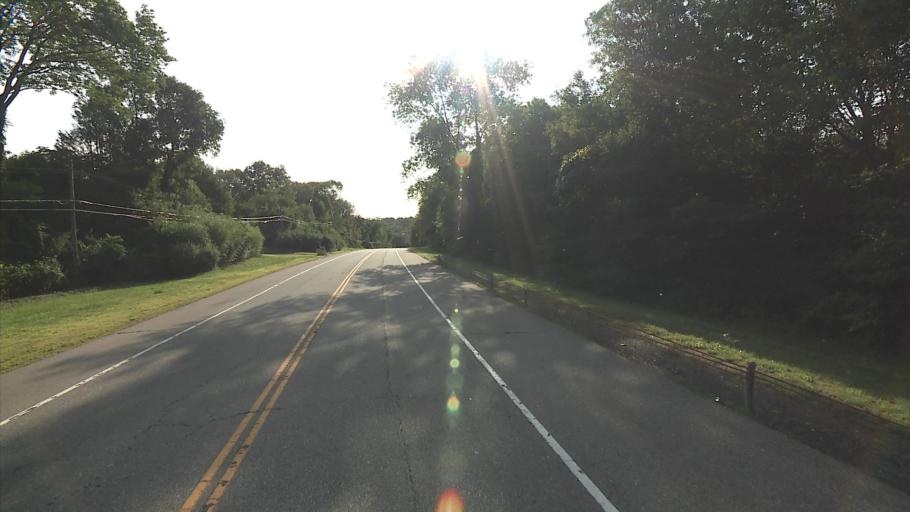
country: US
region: Connecticut
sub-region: New London County
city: Preston City
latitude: 41.4665
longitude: -71.9244
